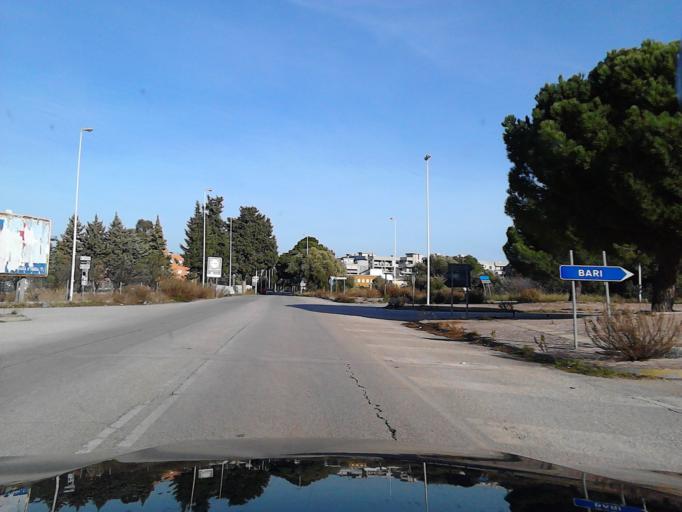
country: IT
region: Apulia
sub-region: Provincia di Bari
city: Mola di Bari
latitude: 41.0517
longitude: 17.0755
